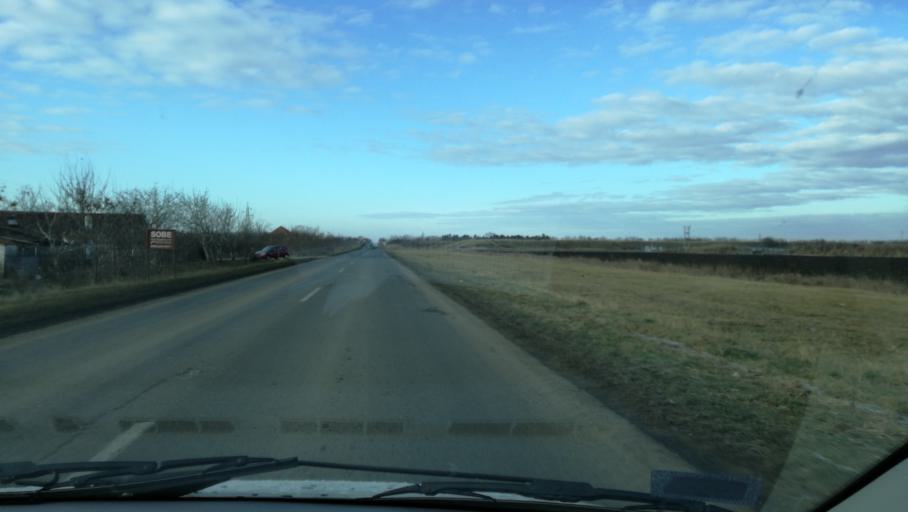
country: RS
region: Autonomna Pokrajina Vojvodina
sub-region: Severnobanatski Okrug
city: Kikinda
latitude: 45.8227
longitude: 20.4214
